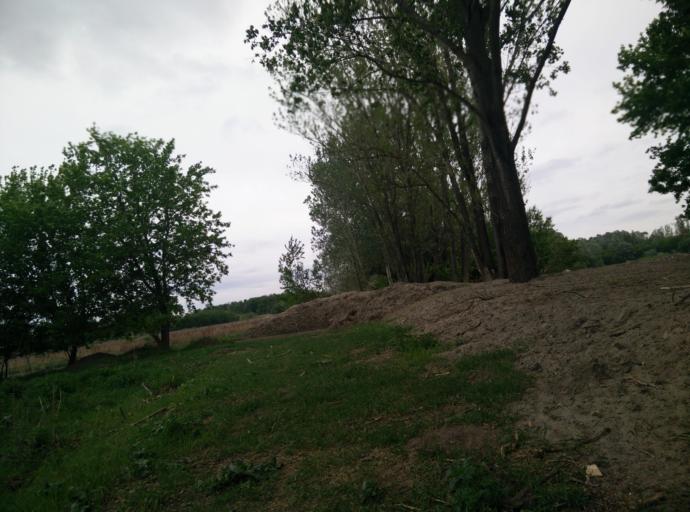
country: HU
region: Pest
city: Dunakeszi
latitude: 47.6016
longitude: 19.1404
